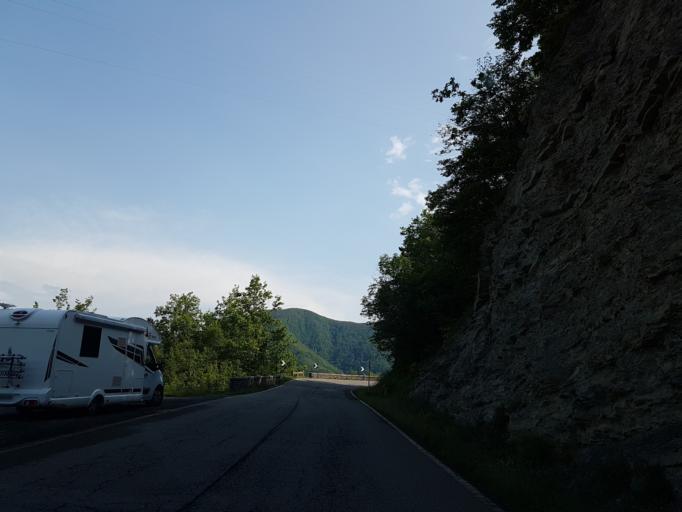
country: IT
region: Emilia-Romagna
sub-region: Forli-Cesena
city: San Piero in Bagno
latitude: 43.8132
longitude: 11.9370
